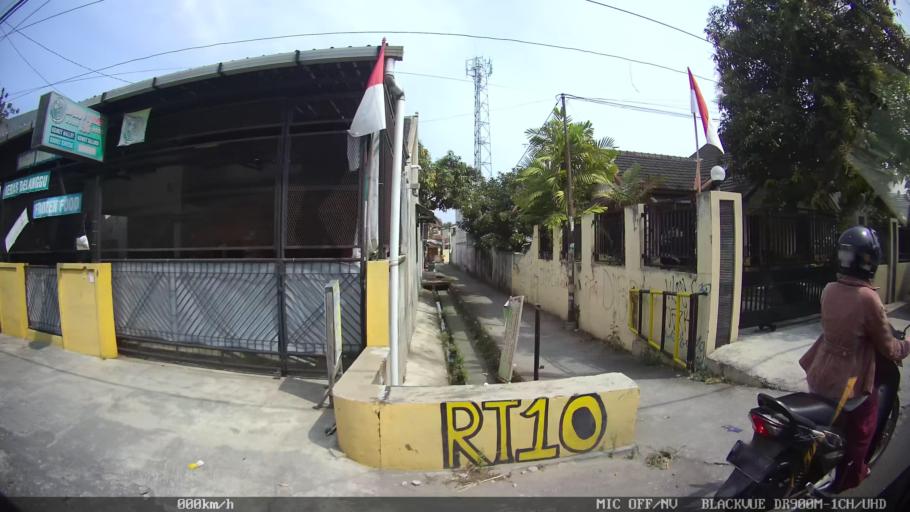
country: ID
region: Daerah Istimewa Yogyakarta
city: Depok
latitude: -7.7986
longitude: 110.4108
